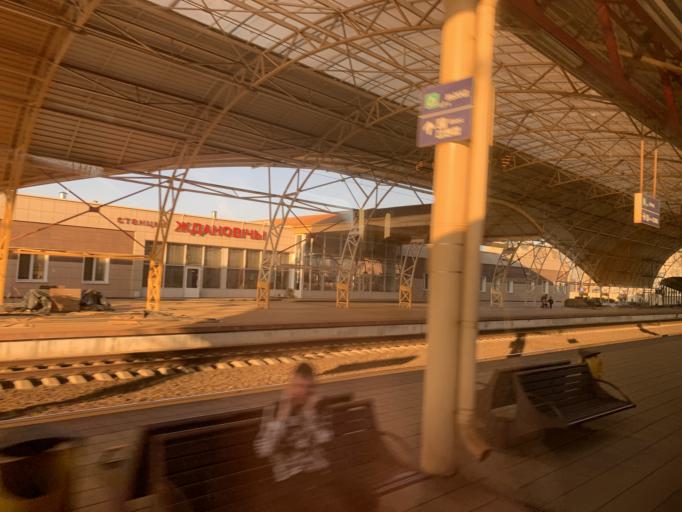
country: BY
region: Minsk
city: Zhdanovichy
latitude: 53.9472
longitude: 27.4260
